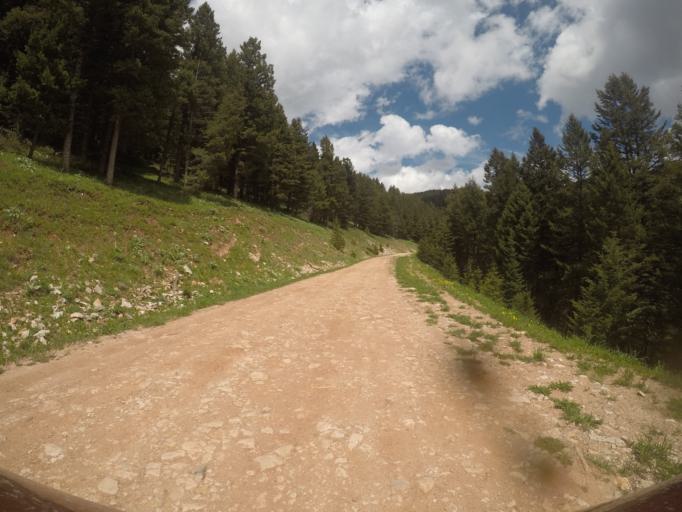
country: US
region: Wyoming
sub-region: Big Horn County
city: Lovell
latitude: 45.1695
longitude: -108.4152
